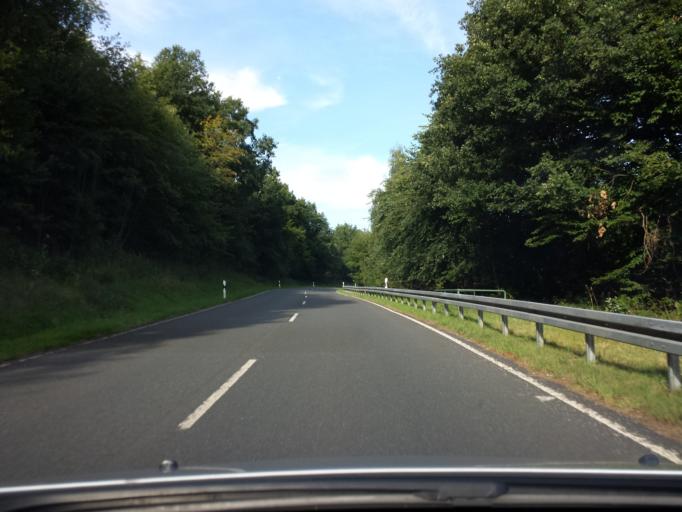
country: DE
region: Hesse
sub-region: Regierungsbezirk Kassel
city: Bad Hersfeld
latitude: 50.8702
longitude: 9.6715
